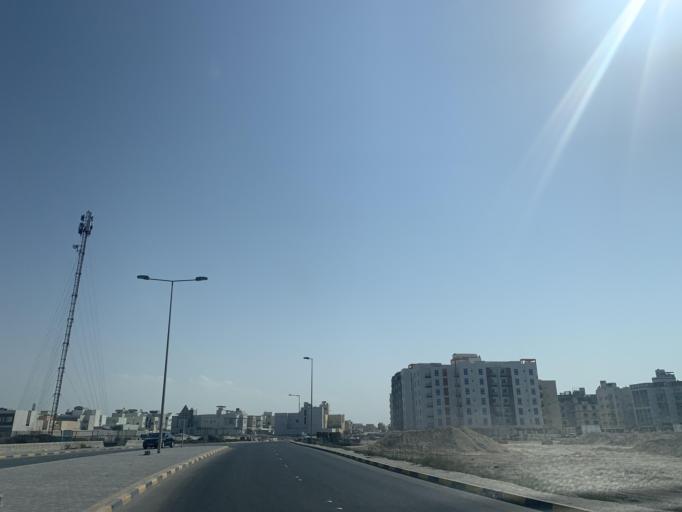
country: BH
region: Central Governorate
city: Madinat Hamad
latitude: 26.1391
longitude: 50.4886
